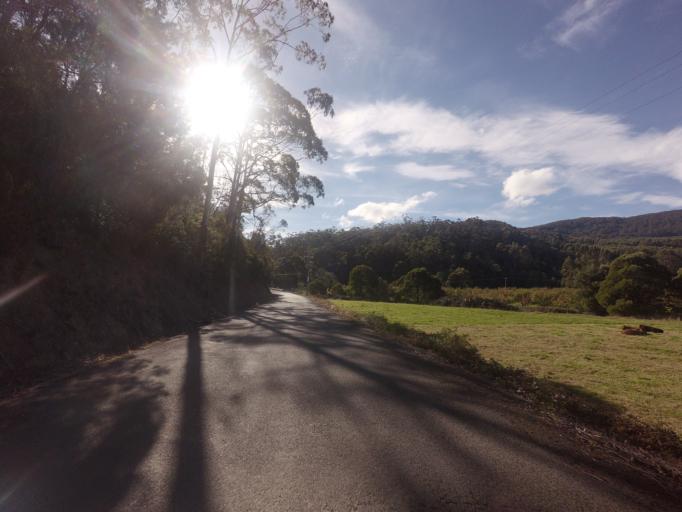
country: AU
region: Tasmania
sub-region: Clarence
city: Sandford
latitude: -43.1200
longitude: 147.7587
